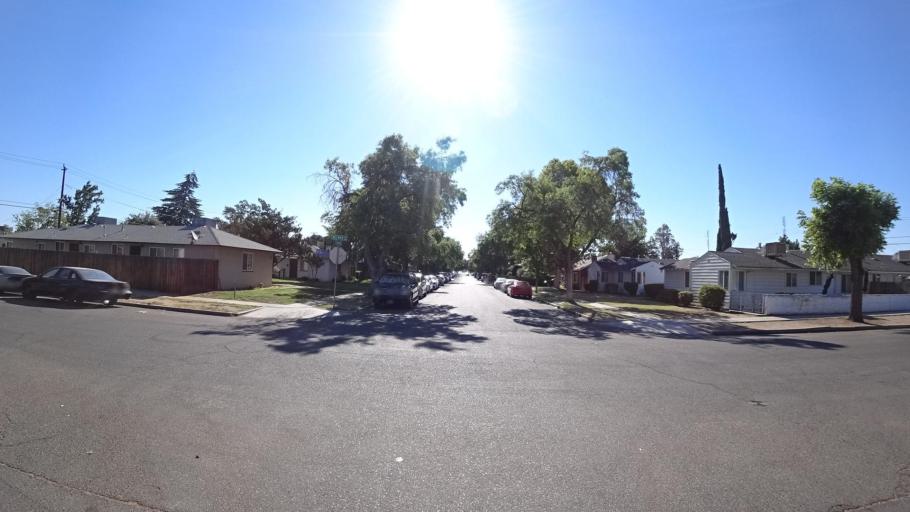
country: US
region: California
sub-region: Fresno County
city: Fresno
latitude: 36.7741
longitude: -119.7951
